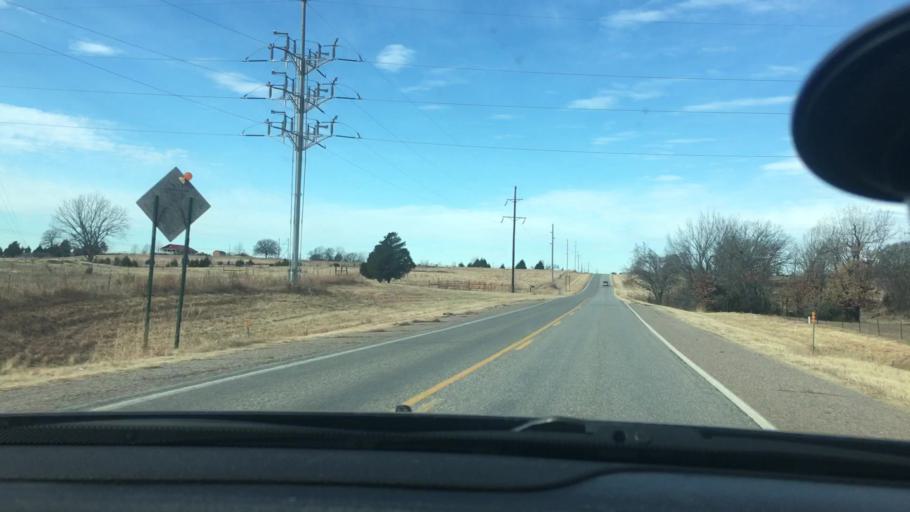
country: US
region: Oklahoma
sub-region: Seminole County
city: Konawa
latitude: 34.9418
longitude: -96.6888
